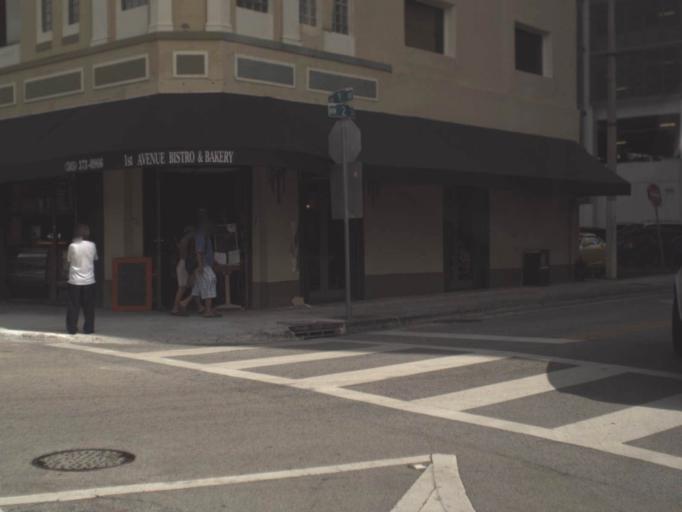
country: US
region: Florida
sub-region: Miami-Dade County
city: Miami
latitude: 25.7760
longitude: -80.1952
